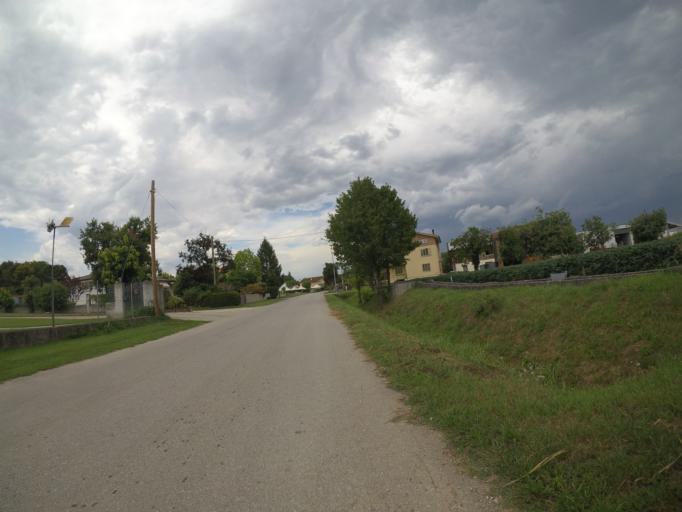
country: IT
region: Friuli Venezia Giulia
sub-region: Provincia di Udine
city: Talmassons
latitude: 45.9270
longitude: 13.1085
